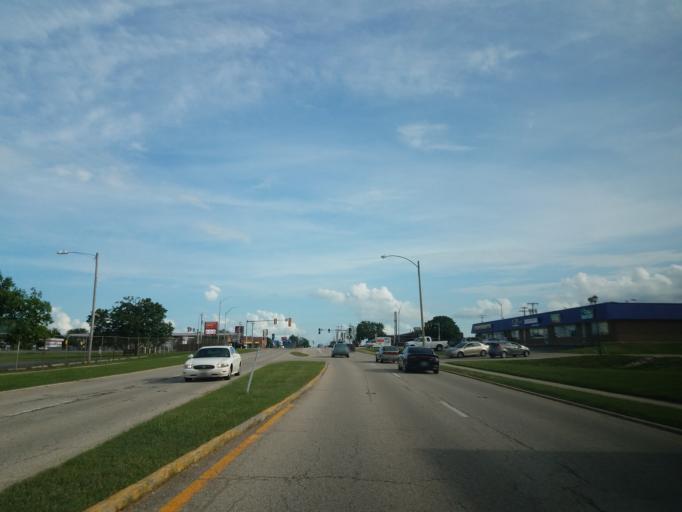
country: US
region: Illinois
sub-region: McLean County
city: Bloomington
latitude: 40.4900
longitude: -88.9432
